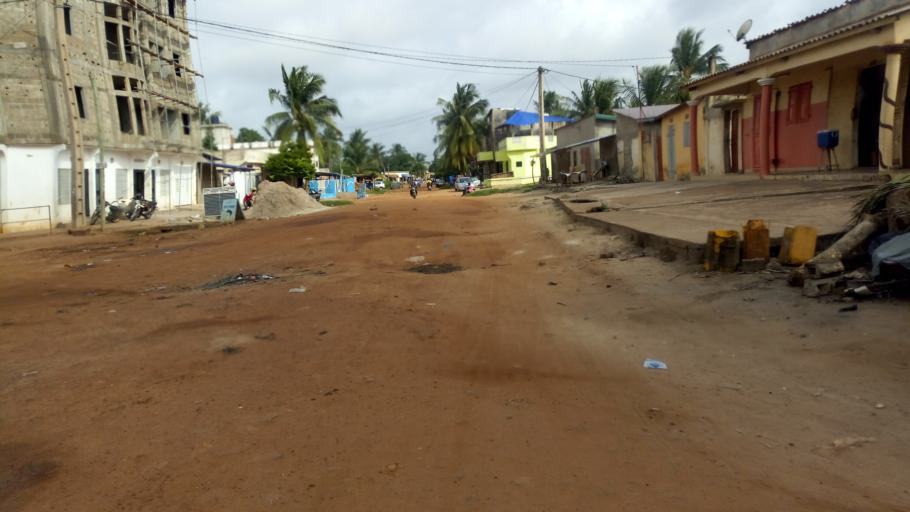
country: TG
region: Maritime
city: Lome
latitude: 6.1756
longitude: 1.1705
